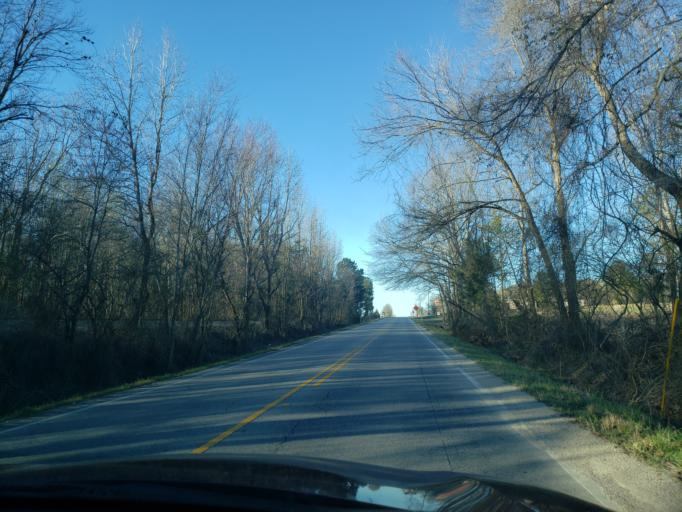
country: US
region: Alabama
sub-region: Lee County
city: Auburn
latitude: 32.6020
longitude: -85.6073
